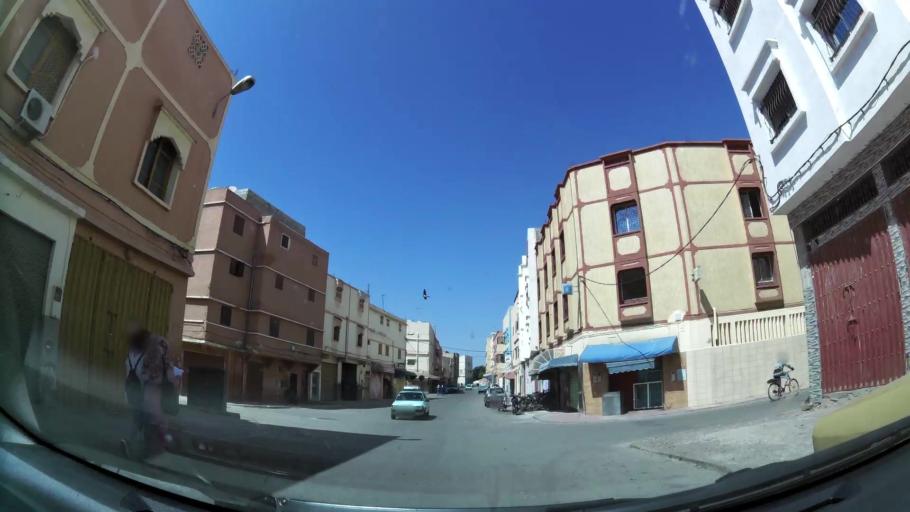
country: MA
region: Souss-Massa-Draa
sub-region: Inezgane-Ait Mellou
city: Inezgane
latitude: 30.3493
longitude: -9.5379
